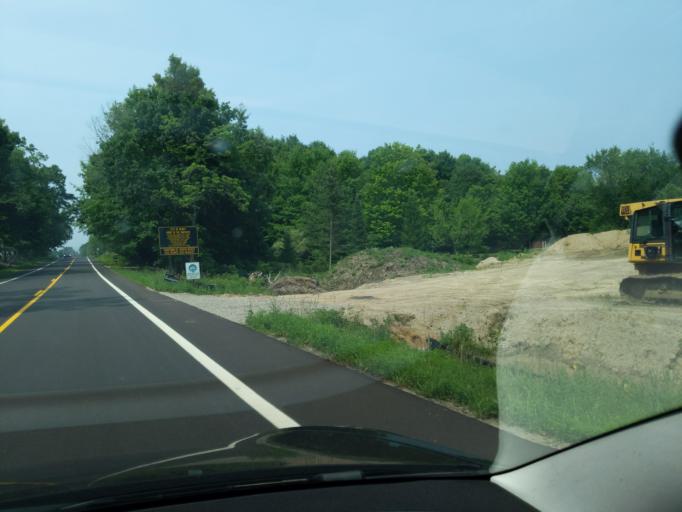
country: US
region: Michigan
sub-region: Clinton County
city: DeWitt
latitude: 42.8215
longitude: -84.5724
